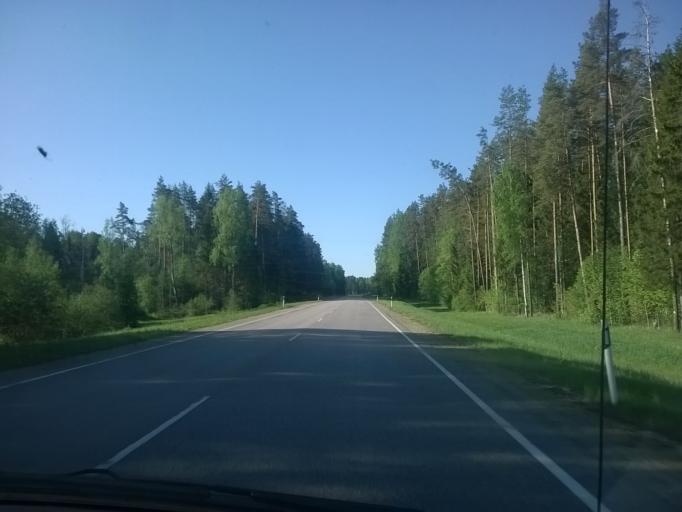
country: EE
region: Valgamaa
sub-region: Valga linn
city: Valga
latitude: 57.8923
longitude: 26.1655
